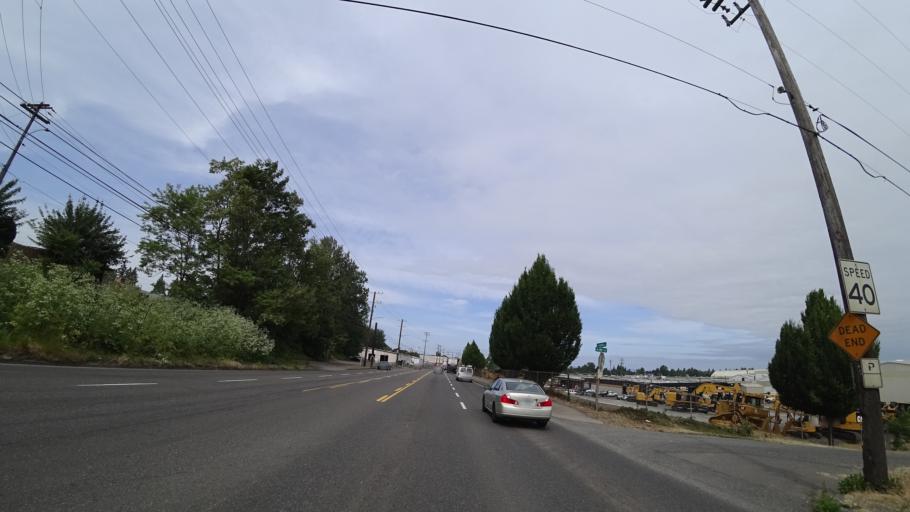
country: US
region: Oregon
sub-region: Multnomah County
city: Portland
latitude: 45.5709
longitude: -122.6155
